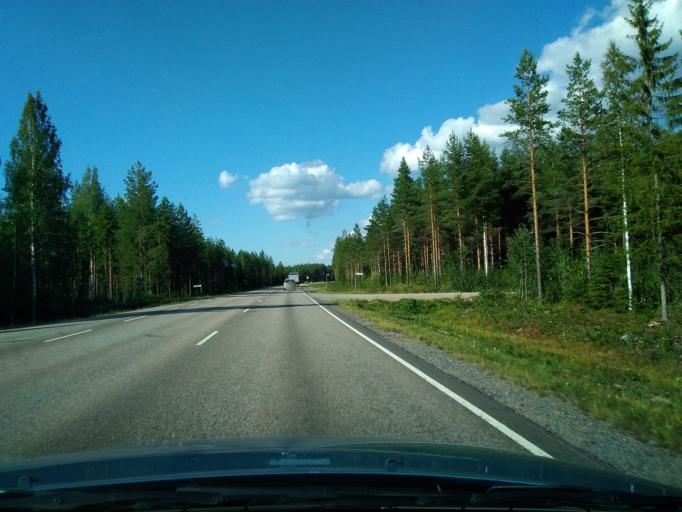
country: FI
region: Pirkanmaa
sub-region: Ylae-Pirkanmaa
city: Maenttae
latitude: 62.0656
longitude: 24.7203
